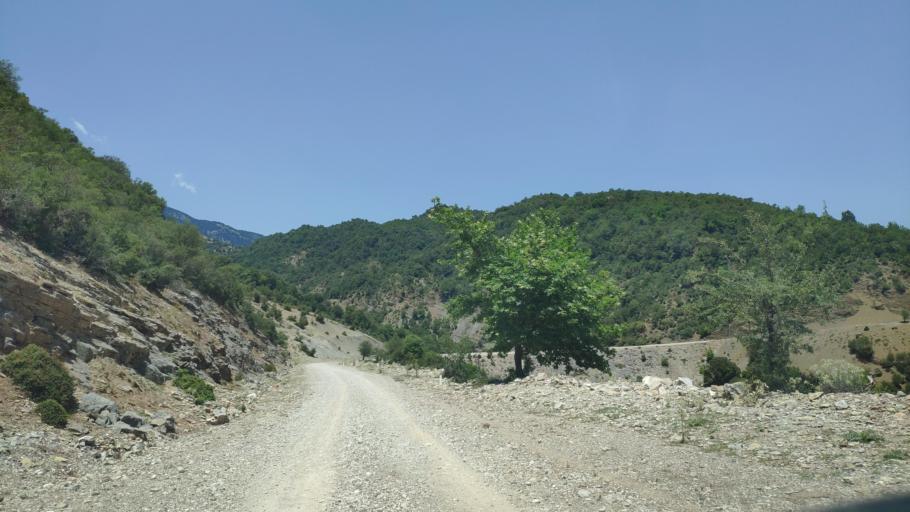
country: GR
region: Thessaly
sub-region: Nomos Kardhitsas
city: Anthiro
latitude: 39.1657
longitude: 21.3721
